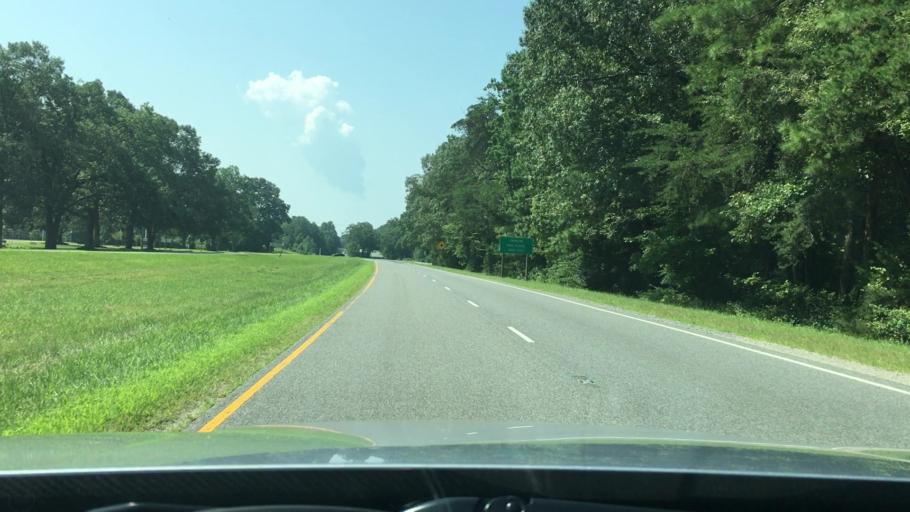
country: US
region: Virginia
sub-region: Caroline County
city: Bowling Green
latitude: 38.0013
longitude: -77.4159
